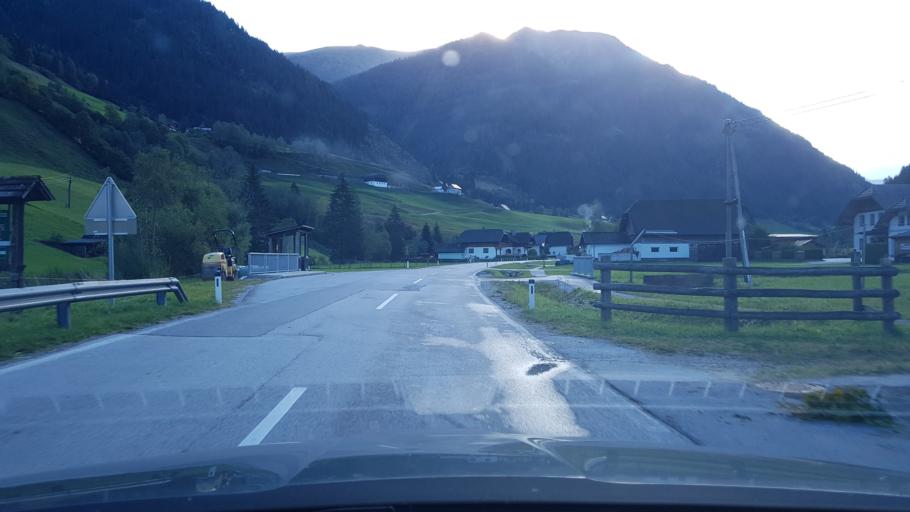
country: AT
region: Styria
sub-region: Politischer Bezirk Liezen
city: Grosssolk
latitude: 47.3763
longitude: 14.0033
